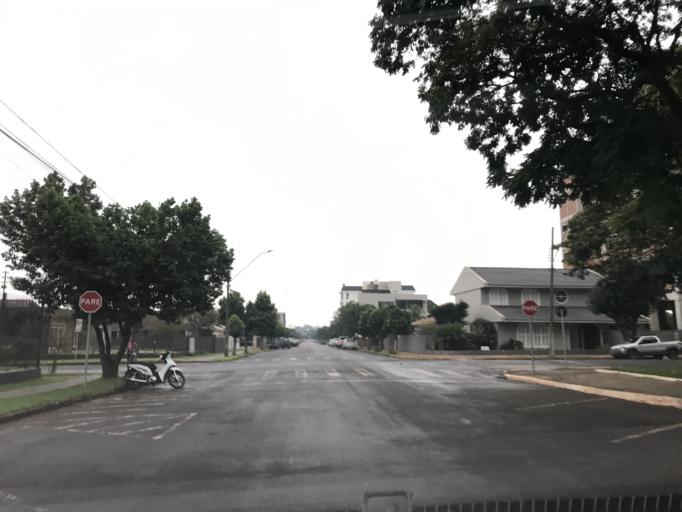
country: BR
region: Parana
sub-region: Palotina
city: Palotina
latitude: -24.2811
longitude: -53.8393
